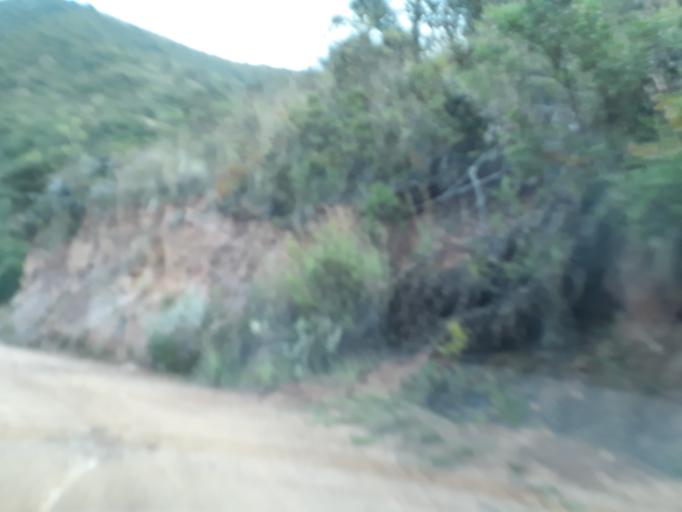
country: CO
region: Boyaca
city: Santa Rosa de Viterbo
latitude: 5.8600
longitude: -72.9694
